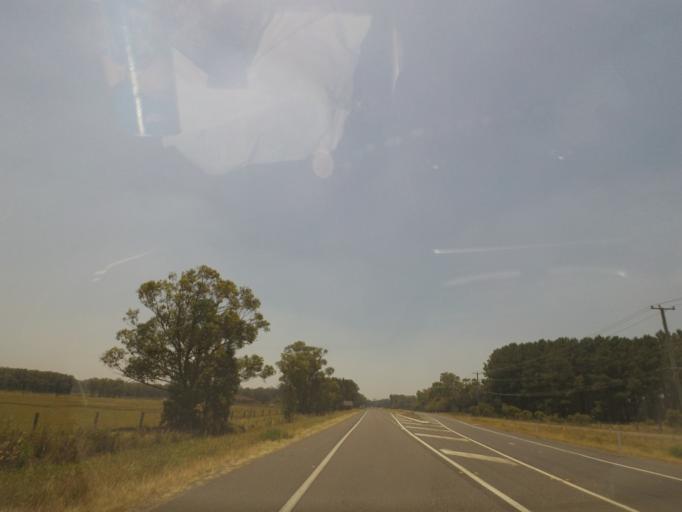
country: AU
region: New South Wales
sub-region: Port Stephens Shire
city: Medowie
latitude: -32.7940
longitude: 151.8955
